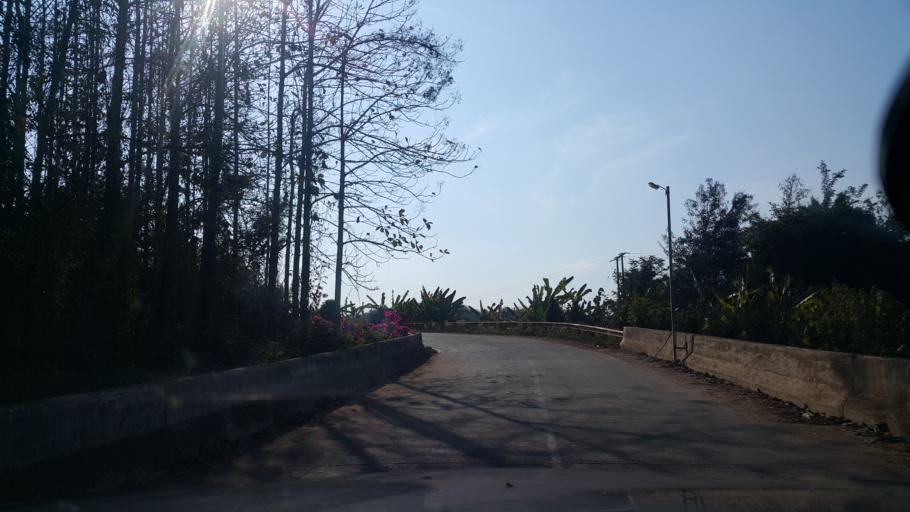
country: TH
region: Loei
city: Chiang Khan
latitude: 17.8031
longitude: 101.6269
